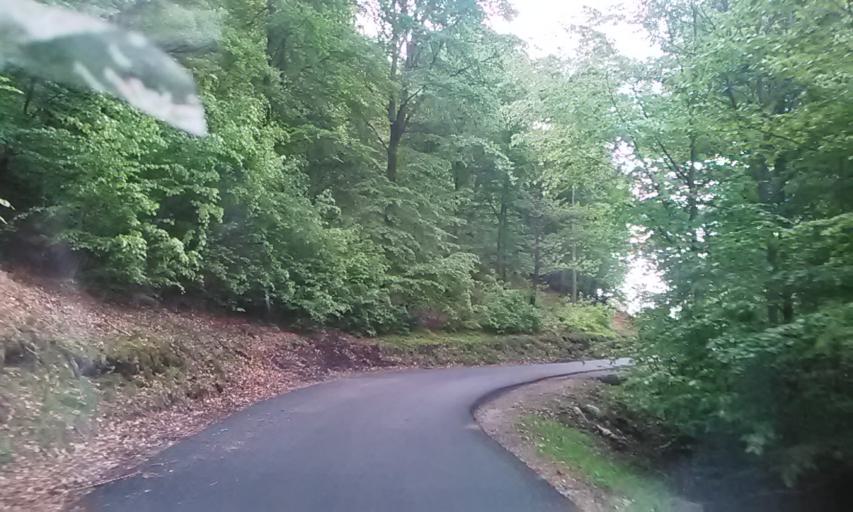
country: IT
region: Piedmont
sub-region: Provincia di Vercelli
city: Breia
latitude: 45.7800
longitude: 8.2962
